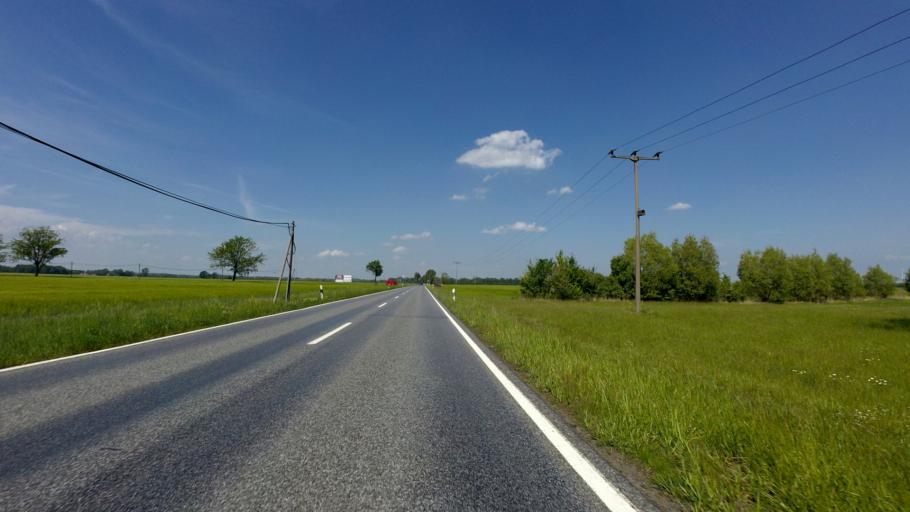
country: DE
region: Brandenburg
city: Luckau
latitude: 51.8340
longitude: 13.7675
